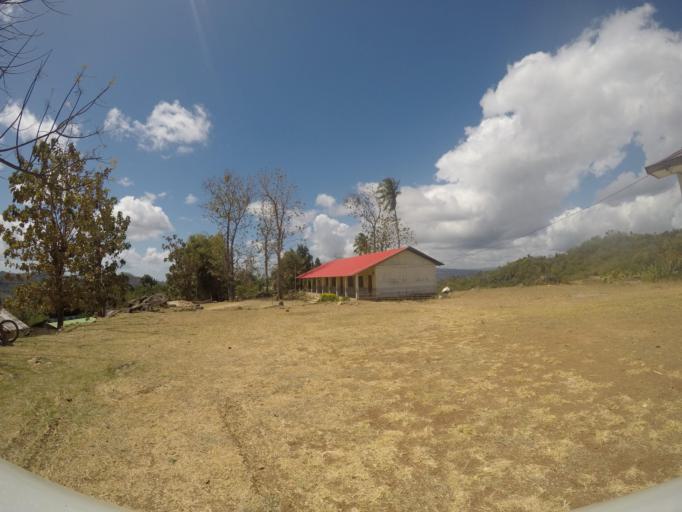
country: TL
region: Lautem
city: Lospalos
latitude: -8.5291
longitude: 126.8008
